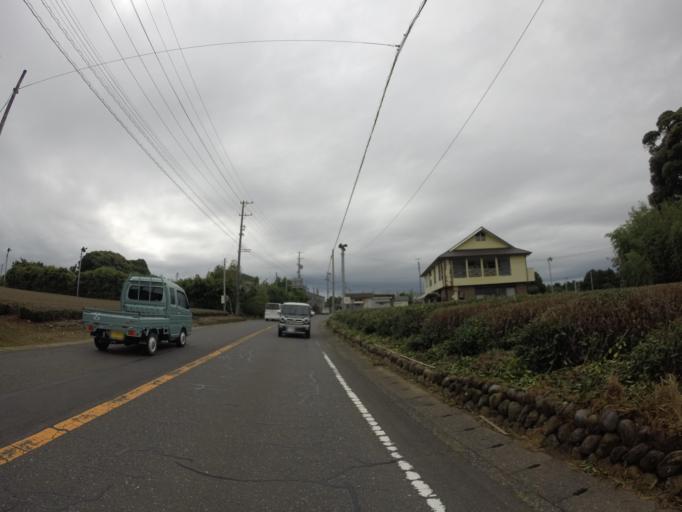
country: JP
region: Shizuoka
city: Sagara
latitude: 34.7347
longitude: 138.1933
